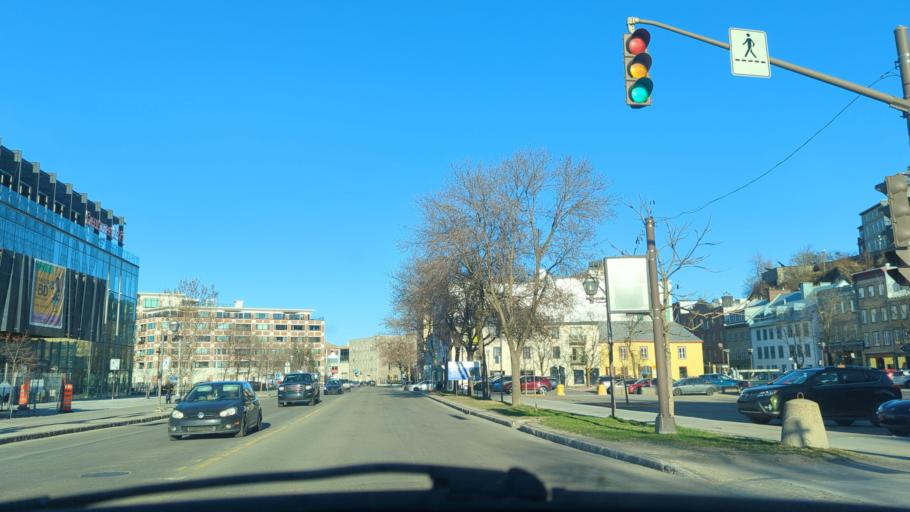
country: CA
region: Quebec
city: Quebec
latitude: 46.8171
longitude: -71.2063
